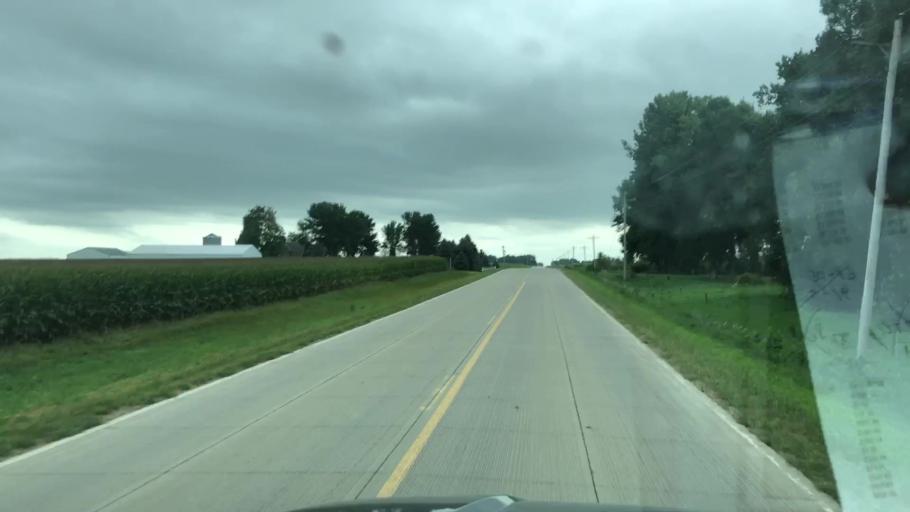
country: US
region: Iowa
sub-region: Sioux County
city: Alton
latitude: 43.0943
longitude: -95.9783
